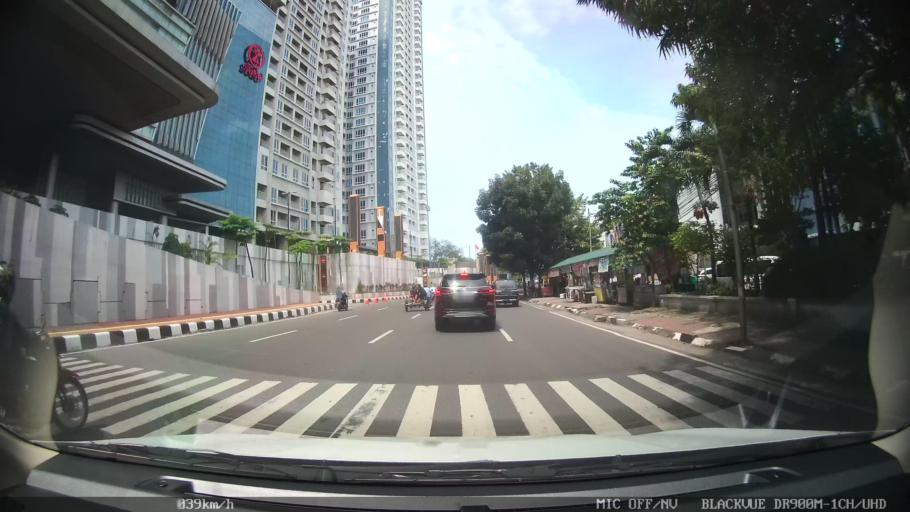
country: ID
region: North Sumatra
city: Medan
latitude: 3.5951
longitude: 98.6746
